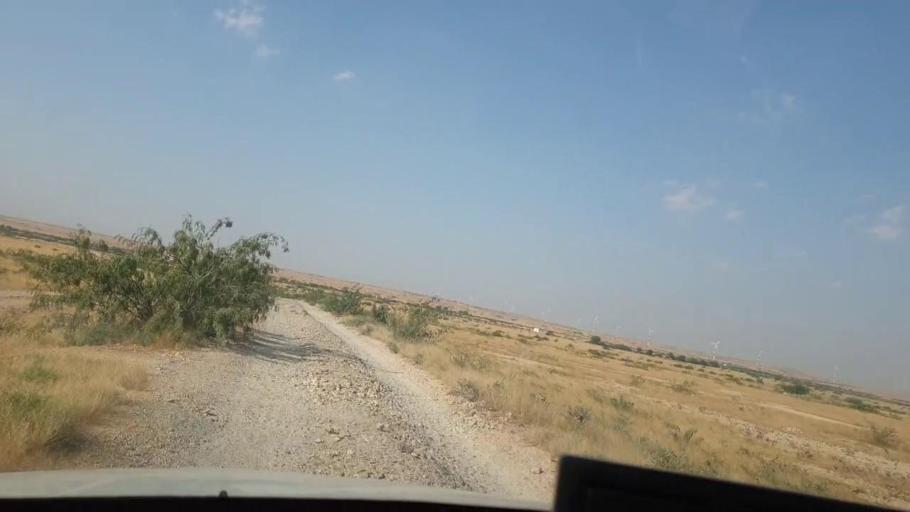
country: PK
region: Sindh
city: Daro Mehar
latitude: 25.0735
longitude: 68.0954
